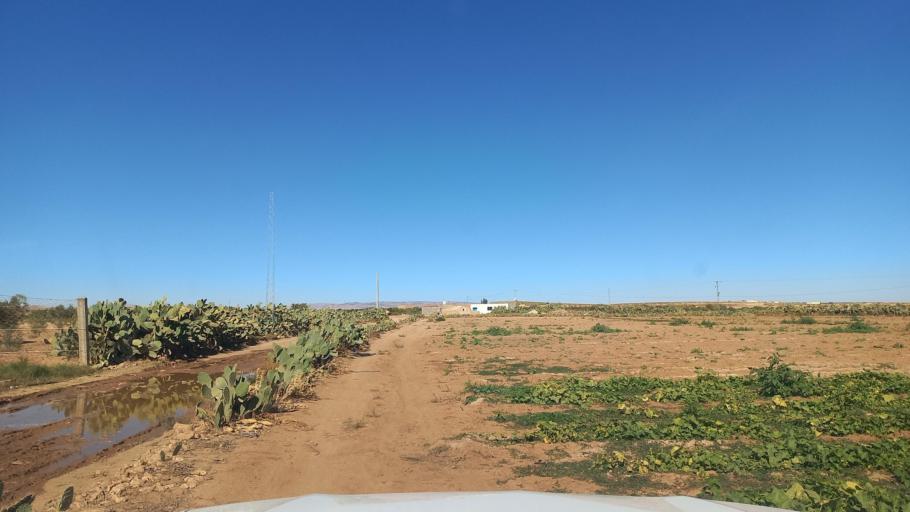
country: TN
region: Al Qasrayn
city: Sbiba
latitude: 35.3933
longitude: 9.0832
